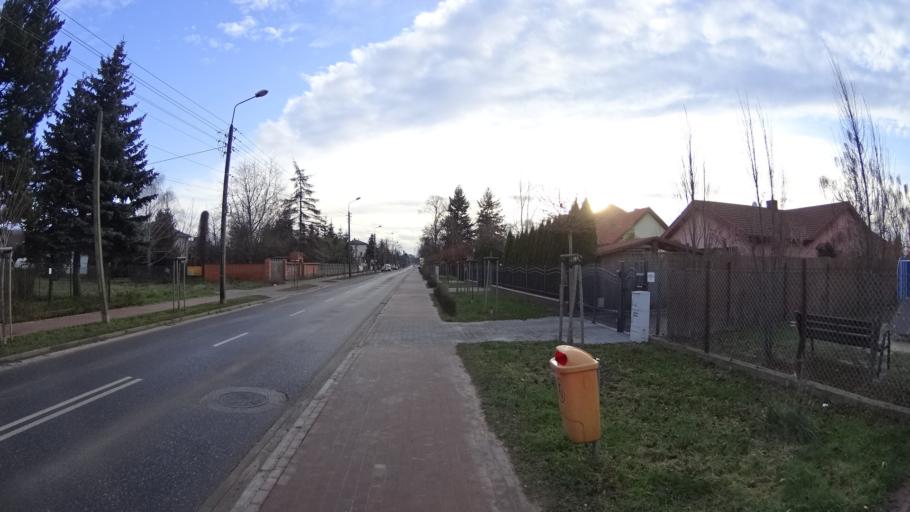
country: PL
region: Masovian Voivodeship
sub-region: Powiat warszawski zachodni
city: Ozarow Mazowiecki
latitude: 52.2201
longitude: 20.8006
